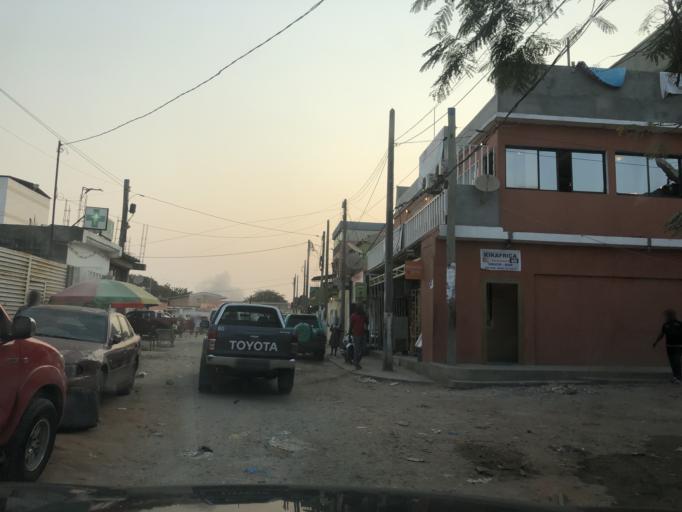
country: AO
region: Luanda
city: Luanda
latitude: -8.8478
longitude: 13.2271
